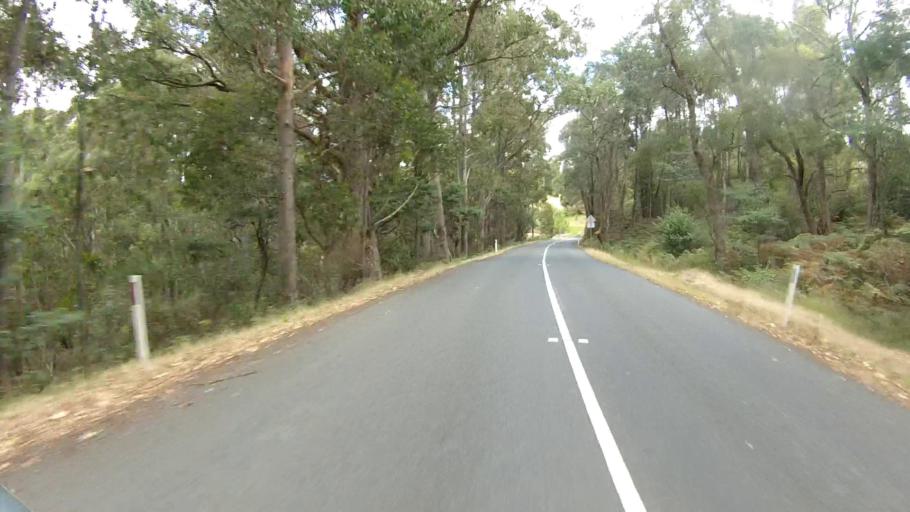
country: AU
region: Tasmania
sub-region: Kingborough
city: Margate
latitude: -42.9709
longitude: 147.1895
